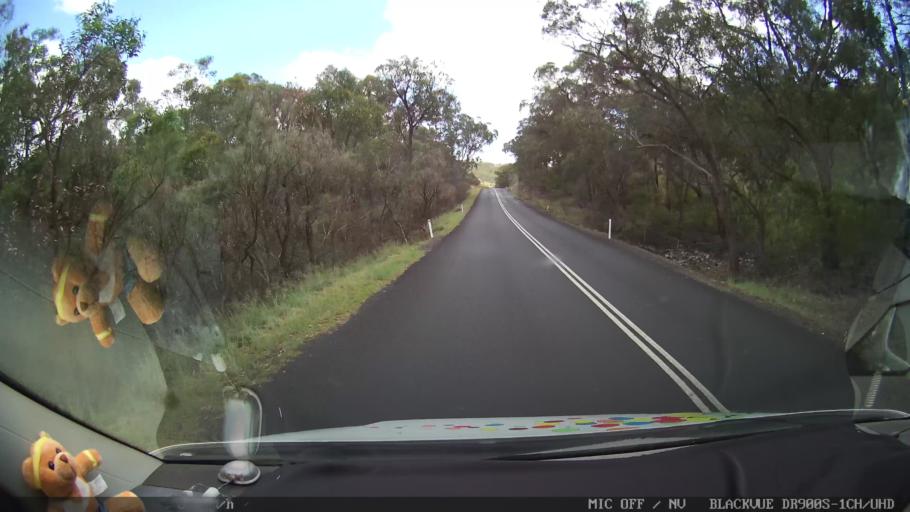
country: AU
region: New South Wales
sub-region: Glen Innes Severn
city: Glen Innes
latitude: -29.5434
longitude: 151.6686
